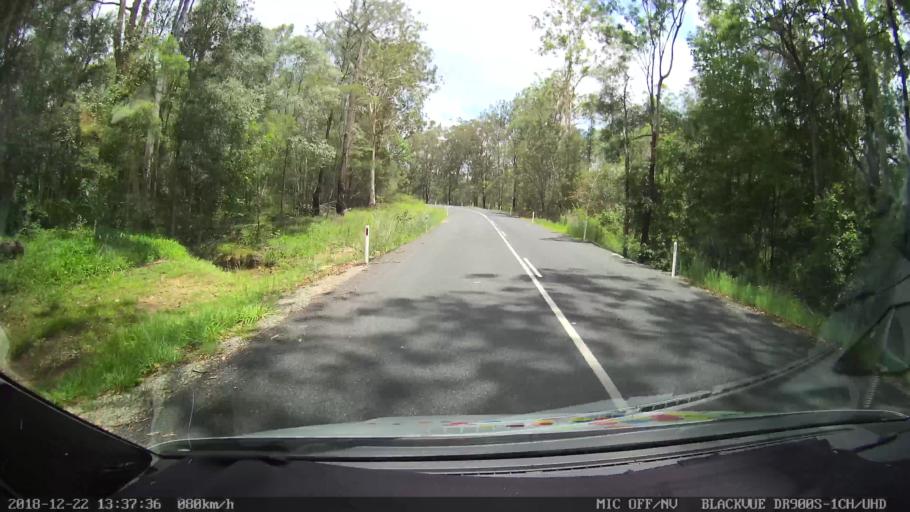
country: AU
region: New South Wales
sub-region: Clarence Valley
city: Coutts Crossing
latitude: -29.8917
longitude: 152.7881
